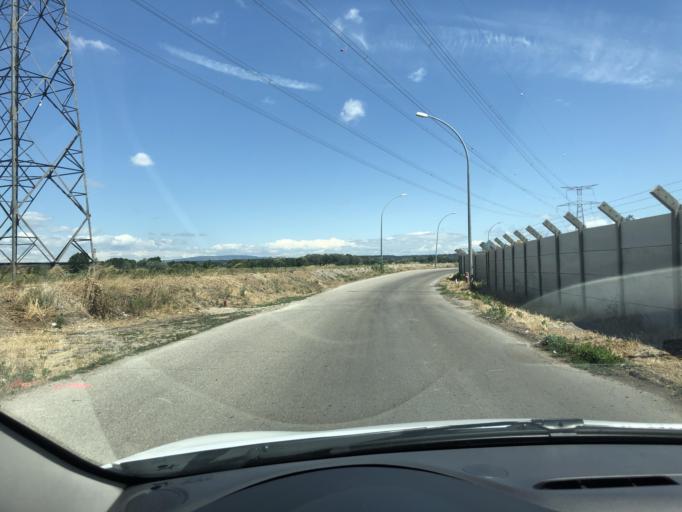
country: FR
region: Provence-Alpes-Cote d'Azur
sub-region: Departement des Bouches-du-Rhone
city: Chateaurenard
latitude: 43.9026
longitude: 4.8729
